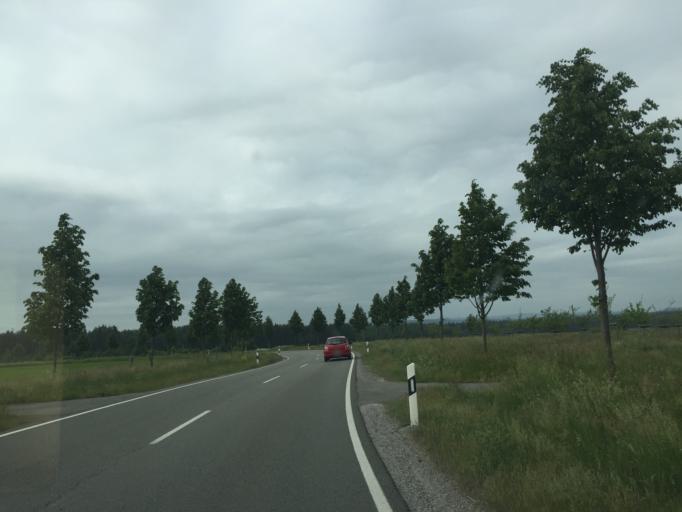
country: DE
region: Thuringia
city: Pennewitz
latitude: 50.6574
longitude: 11.0481
